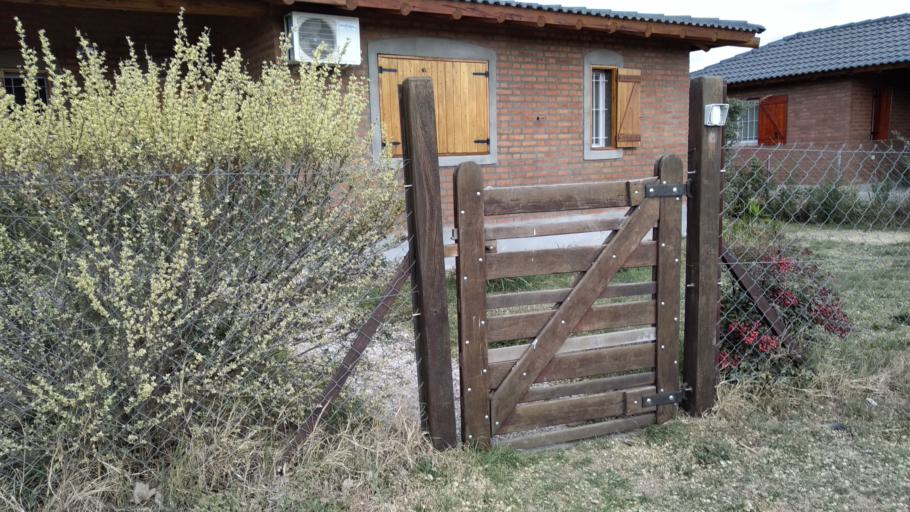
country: AR
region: Cordoba
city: Mina Clavero
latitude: -31.7277
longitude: -65.0220
